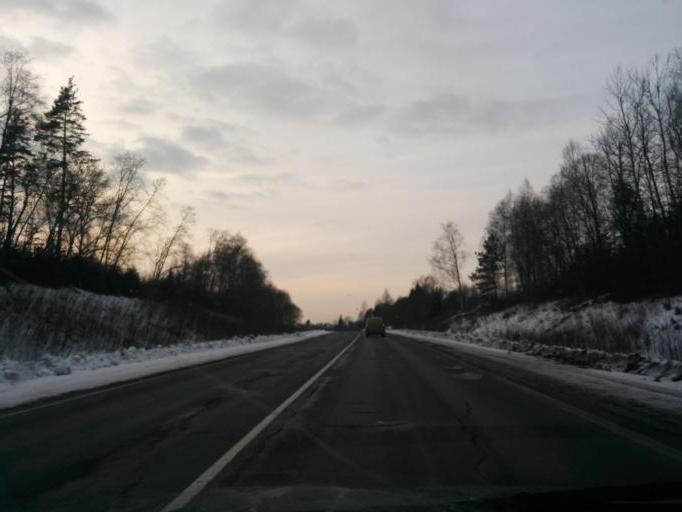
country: LV
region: Raunas
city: Rauna
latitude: 57.3183
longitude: 25.7101
